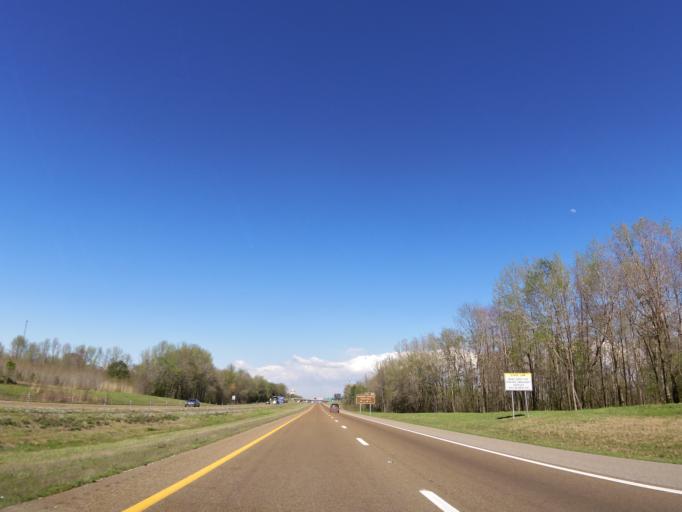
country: US
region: Tennessee
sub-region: Decatur County
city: Parsons
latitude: 35.8356
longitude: -88.0948
